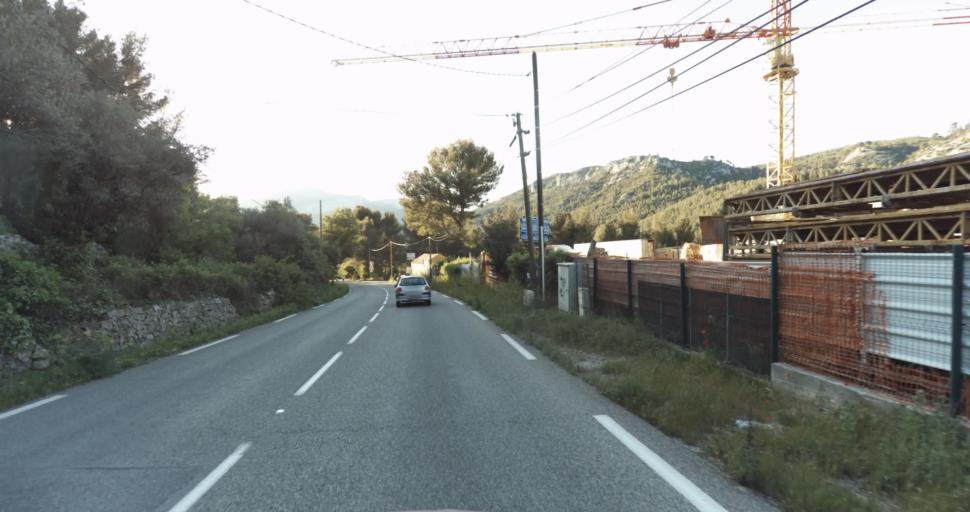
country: FR
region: Provence-Alpes-Cote d'Azur
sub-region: Departement du Var
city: Le Revest-les-Eaux
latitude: 43.1585
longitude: 5.9561
